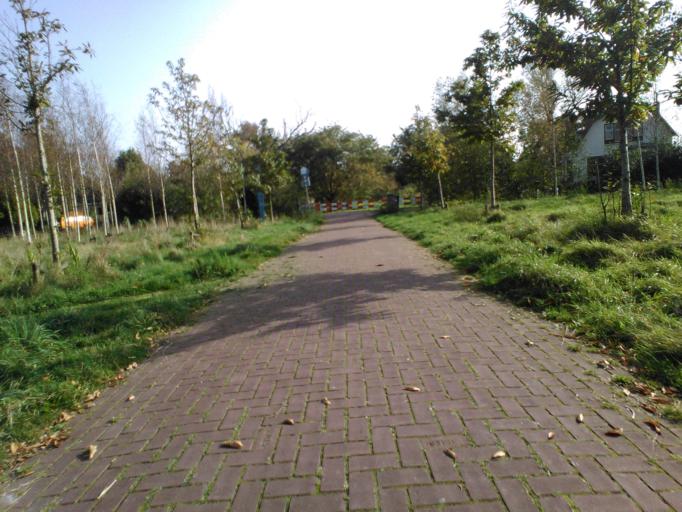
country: NL
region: South Holland
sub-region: Gemeente Leiderdorp
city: Leiderdorp
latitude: 52.1494
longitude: 4.5192
